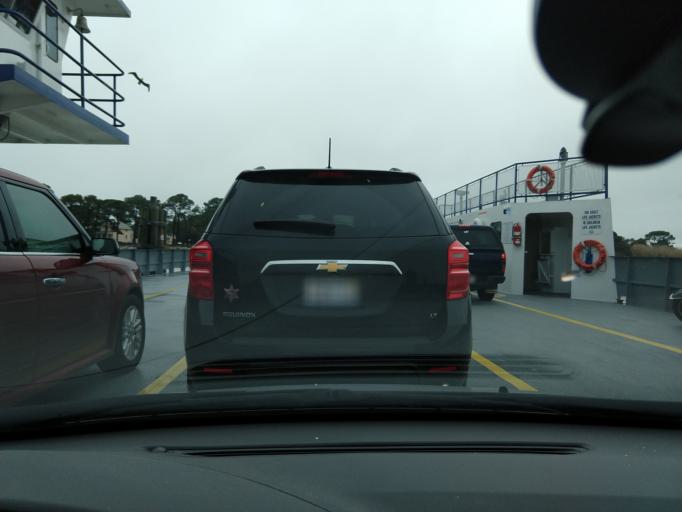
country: US
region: Alabama
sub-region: Mobile County
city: Dauphin Island
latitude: 30.2331
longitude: -88.0157
